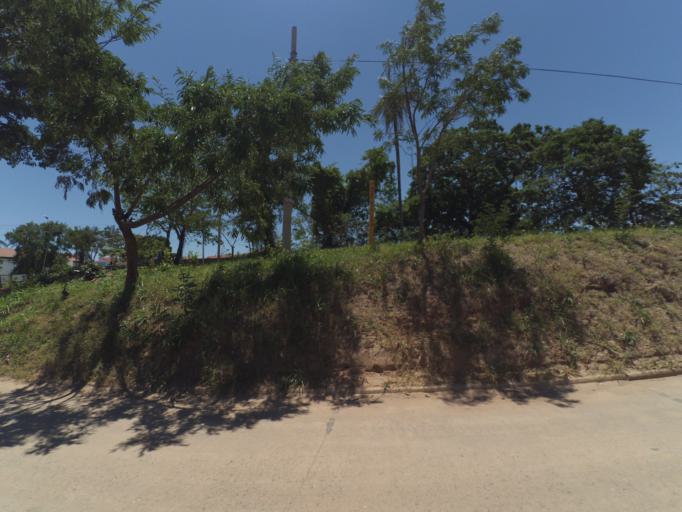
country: BO
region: Santa Cruz
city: Santa Cruz de la Sierra
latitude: -17.7532
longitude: -63.2212
